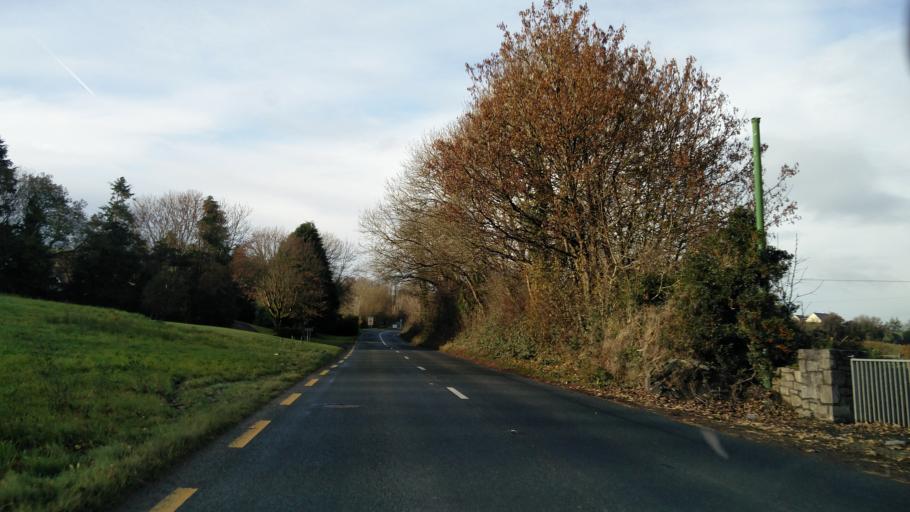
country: IE
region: Connaught
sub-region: Maigh Eo
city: Westport
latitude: 53.7886
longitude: -9.5002
